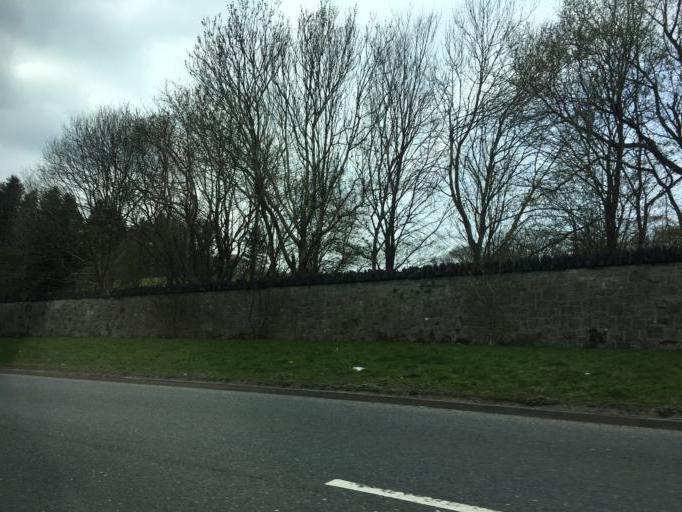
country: GB
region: Wales
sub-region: Gwynedd
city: Y Felinheli
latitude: 53.2001
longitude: -4.1807
